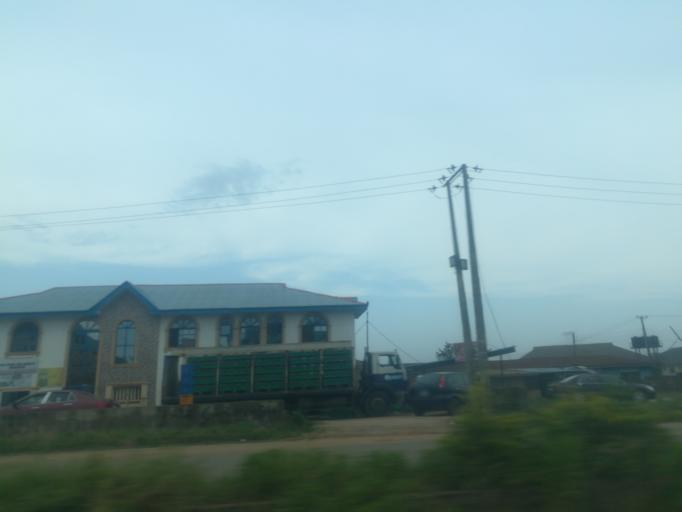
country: NG
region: Oyo
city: Ibadan
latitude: 7.3632
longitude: 3.8231
